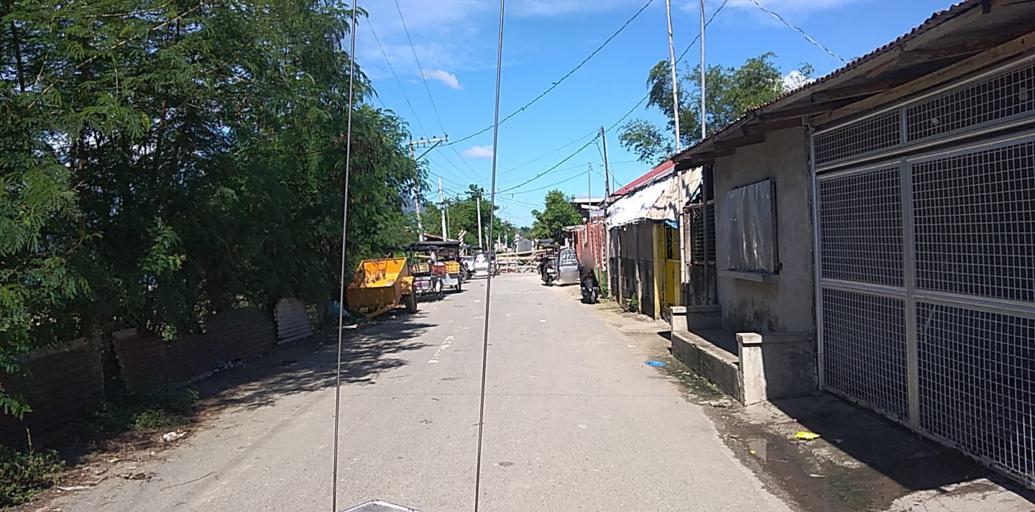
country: PH
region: Central Luzon
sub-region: Province of Pampanga
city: Candating
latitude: 15.1320
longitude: 120.8075
